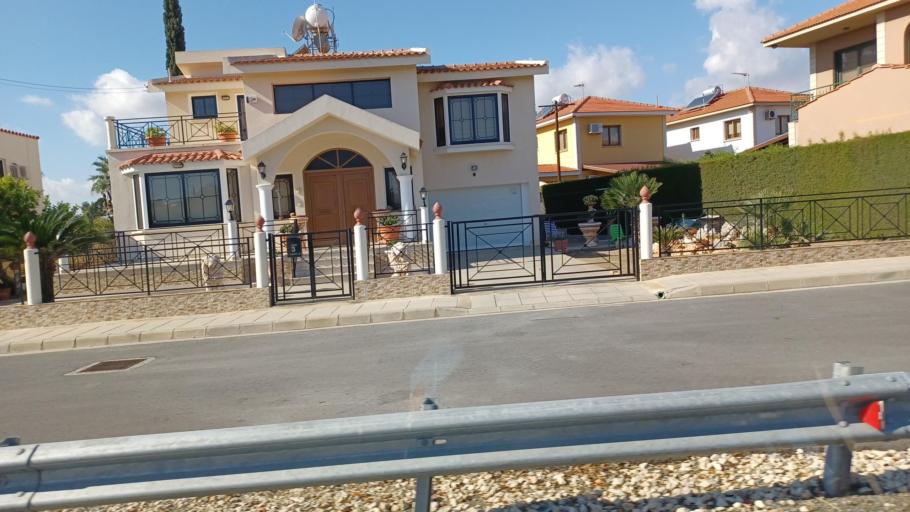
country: CY
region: Larnaka
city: Voroklini
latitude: 34.9805
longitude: 33.6766
